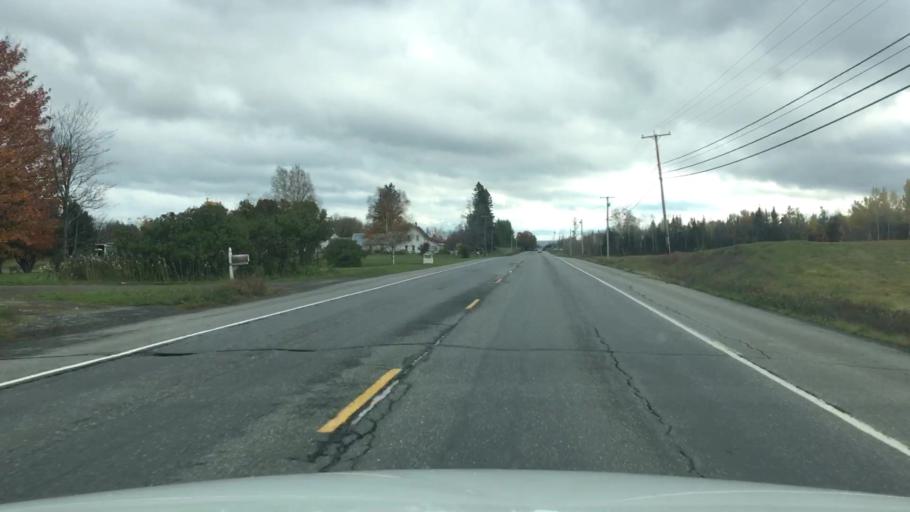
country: US
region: Maine
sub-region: Aroostook County
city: Houlton
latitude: 46.1872
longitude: -67.8412
